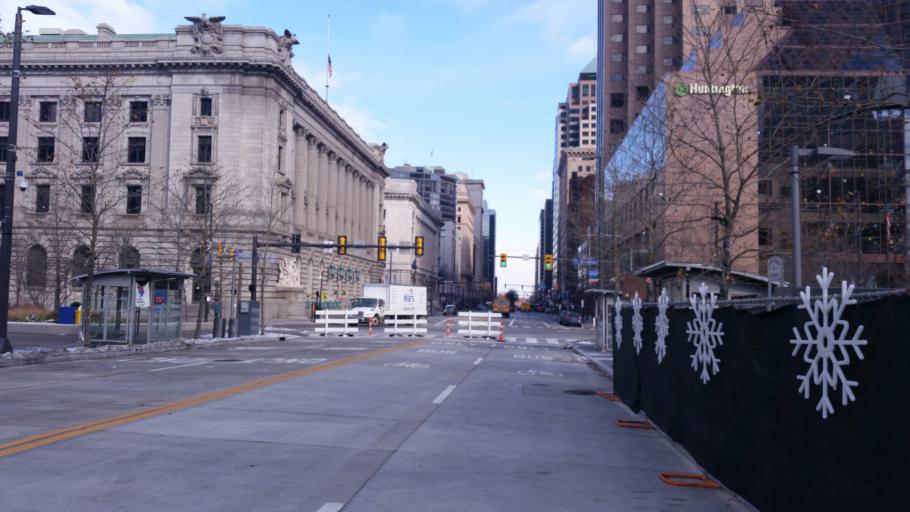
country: US
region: Ohio
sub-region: Cuyahoga County
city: Cleveland
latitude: 41.4999
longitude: -81.6934
